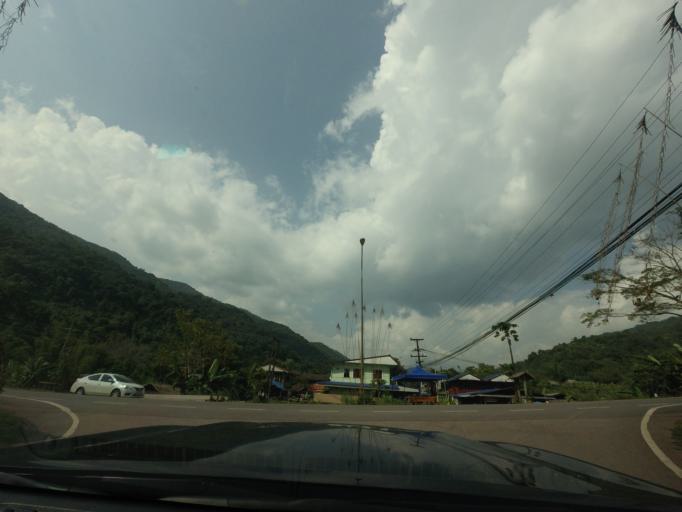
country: TH
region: Nan
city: Bo Kluea
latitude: 19.1520
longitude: 101.1553
